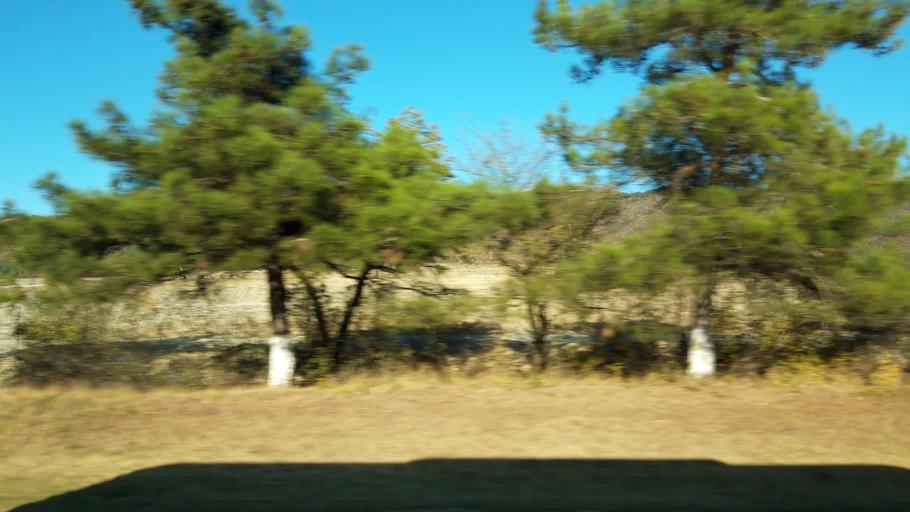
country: RU
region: Krasnodarskiy
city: Kabardinka
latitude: 44.6297
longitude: 38.0035
